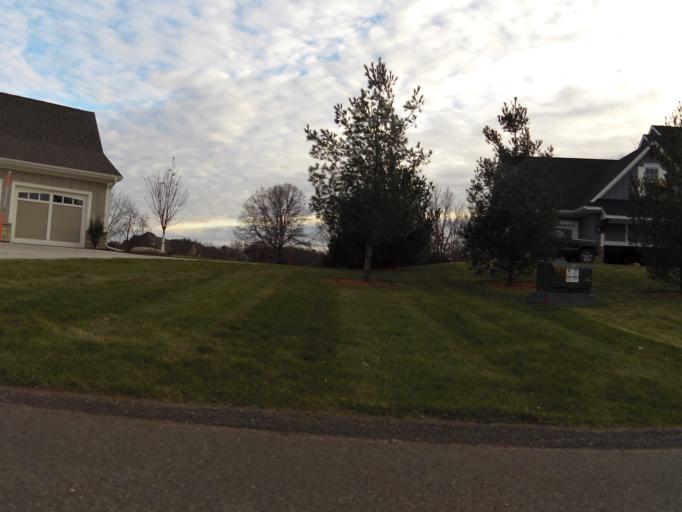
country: US
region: Minnesota
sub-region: Washington County
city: Bayport
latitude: 44.9997
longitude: -92.7984
